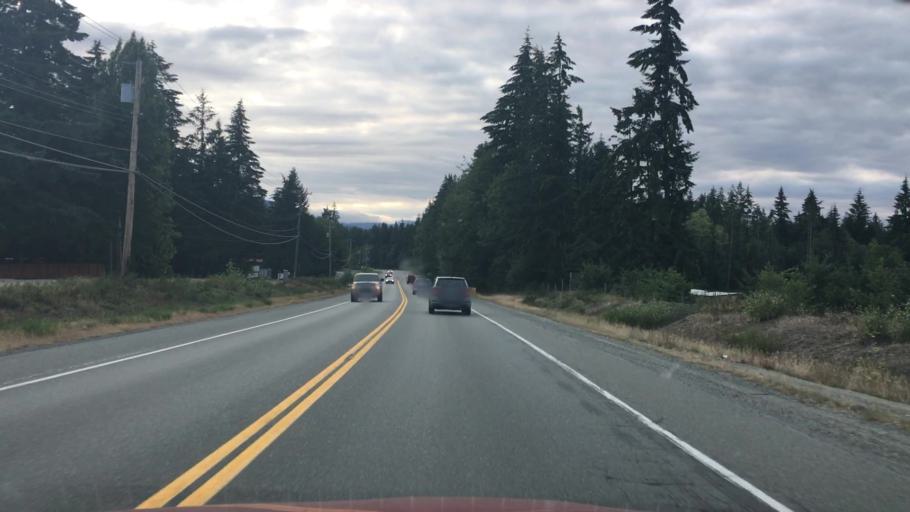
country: CA
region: British Columbia
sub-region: Regional District of Nanaimo
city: Parksville
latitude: 49.3115
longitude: -124.5037
